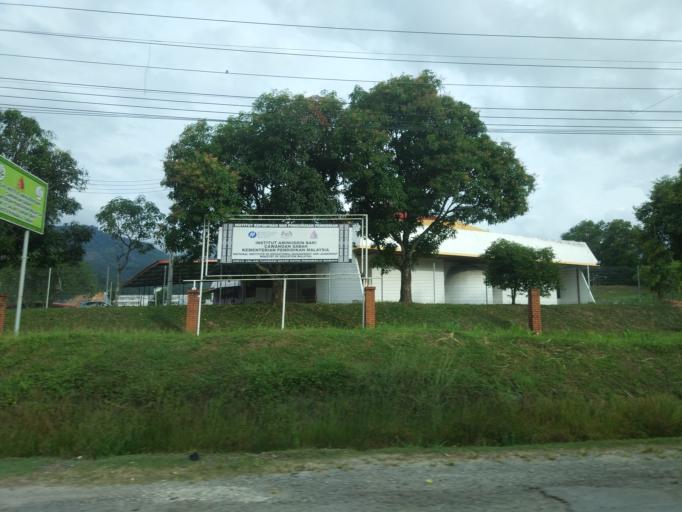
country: MY
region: Sabah
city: Kota Kinabalu
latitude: 6.0585
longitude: 116.1759
